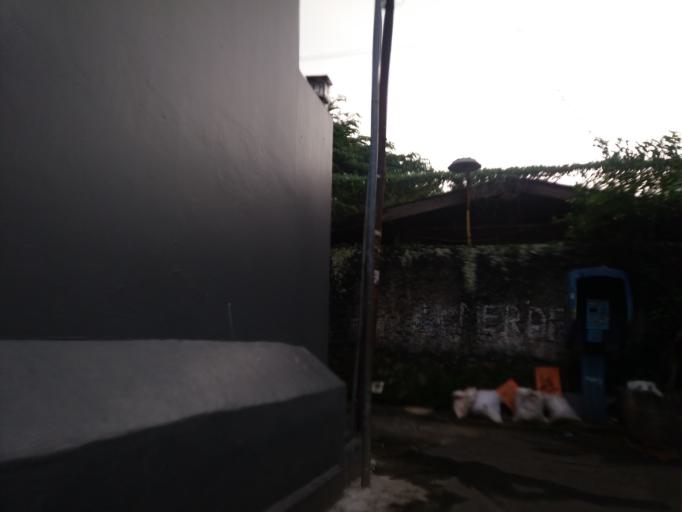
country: ID
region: Jakarta Raya
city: Jakarta
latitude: -6.2168
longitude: 106.8241
